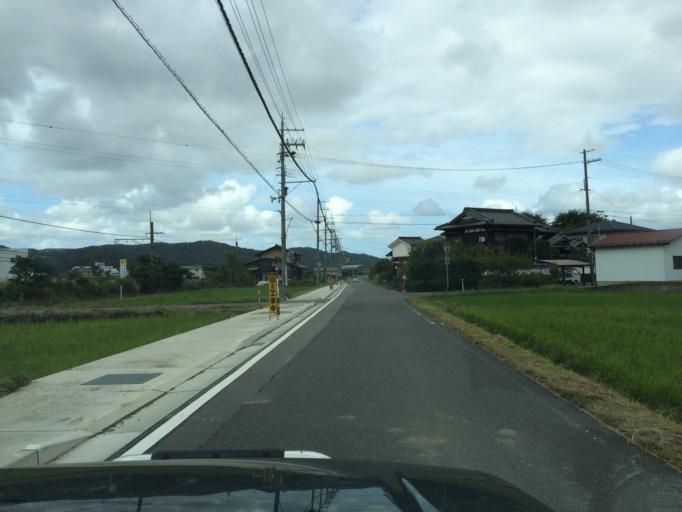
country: JP
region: Hyogo
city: Toyooka
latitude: 35.4769
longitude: 134.7824
